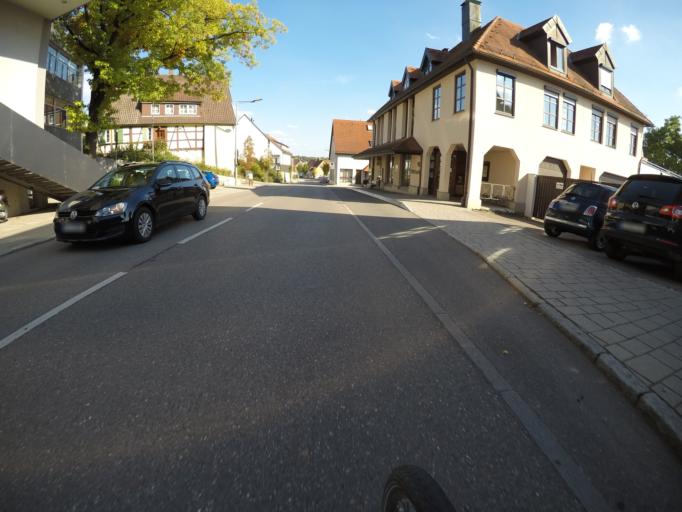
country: DE
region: Baden-Wuerttemberg
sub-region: Regierungsbezirk Stuttgart
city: Denkendorf
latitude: 48.6939
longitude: 9.3179
